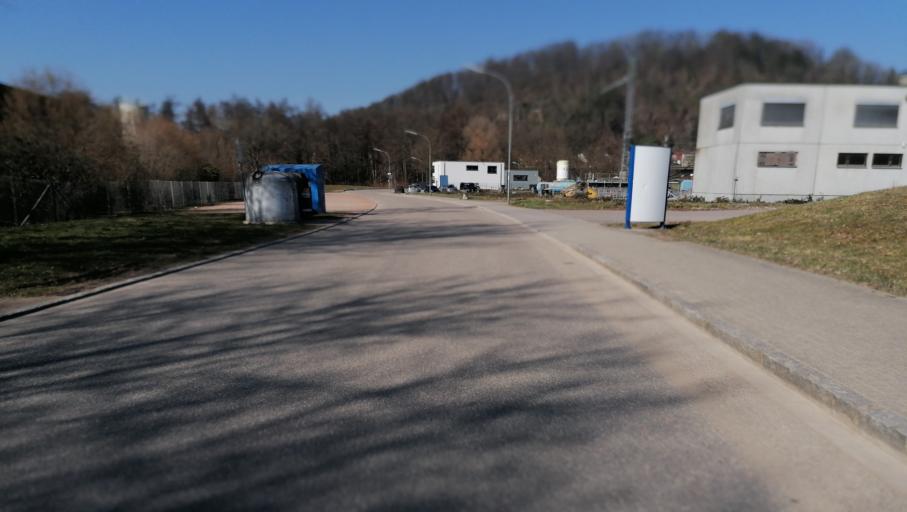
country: DE
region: Baden-Wuerttemberg
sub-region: Freiburg Region
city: Schworstadt
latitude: 47.5817
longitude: 7.9075
